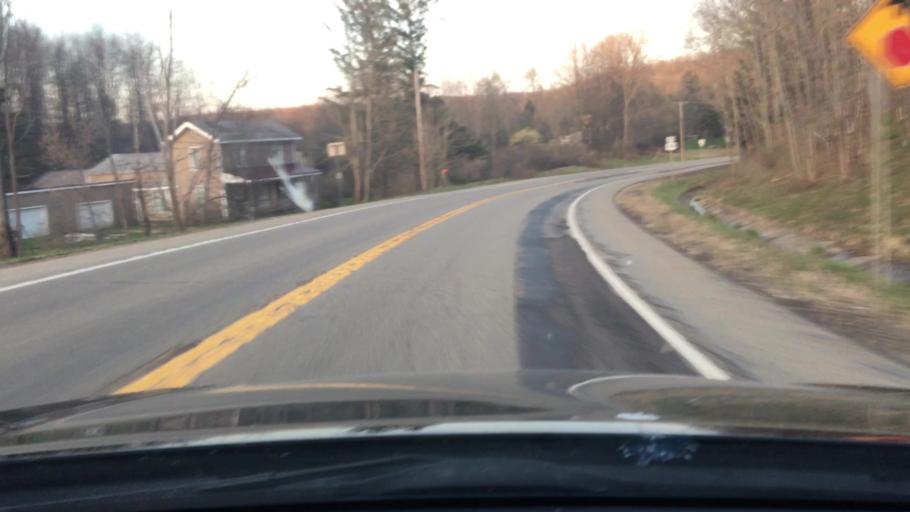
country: US
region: New York
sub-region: Cattaraugus County
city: Randolph
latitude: 42.1712
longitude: -78.9348
